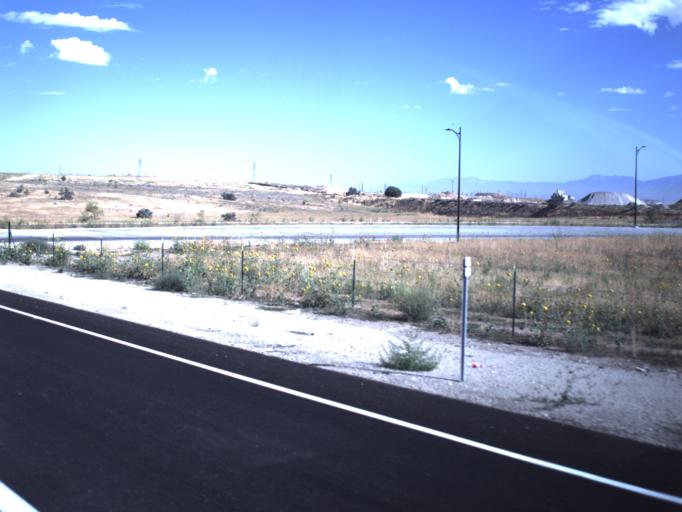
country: US
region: Utah
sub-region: Salt Lake County
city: Oquirrh
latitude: 40.6387
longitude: -112.0593
